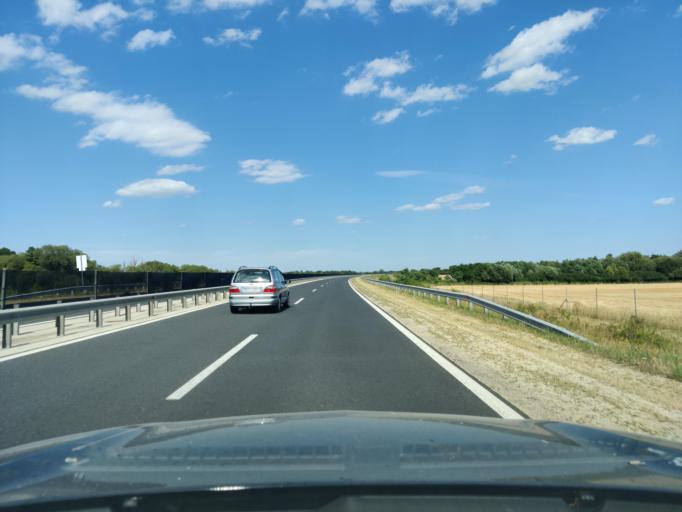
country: HU
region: Vas
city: Vep
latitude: 47.2703
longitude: 16.7547
